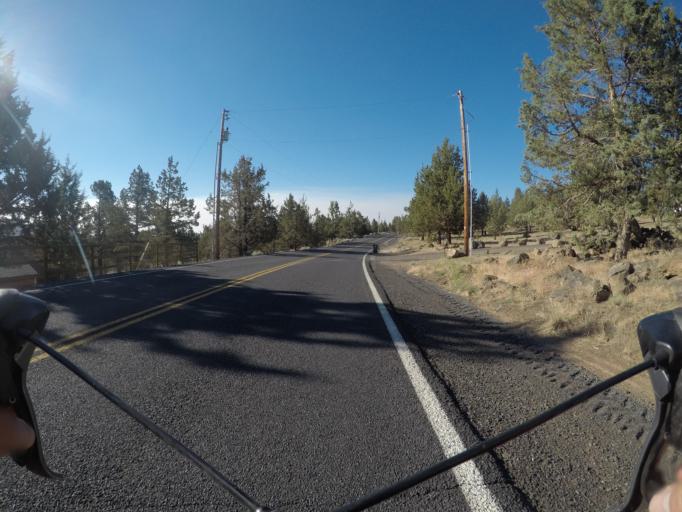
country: US
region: Oregon
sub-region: Deschutes County
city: Redmond
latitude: 44.1801
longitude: -121.2664
